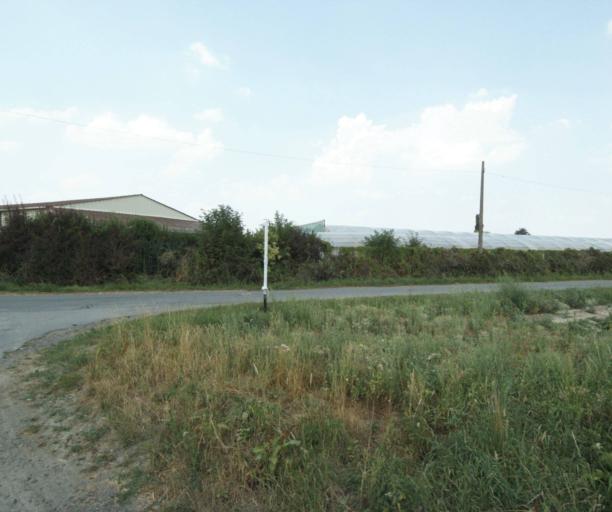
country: FR
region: Nord-Pas-de-Calais
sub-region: Departement du Nord
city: Quesnoy-sur-Deule
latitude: 50.7332
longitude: 3.0237
